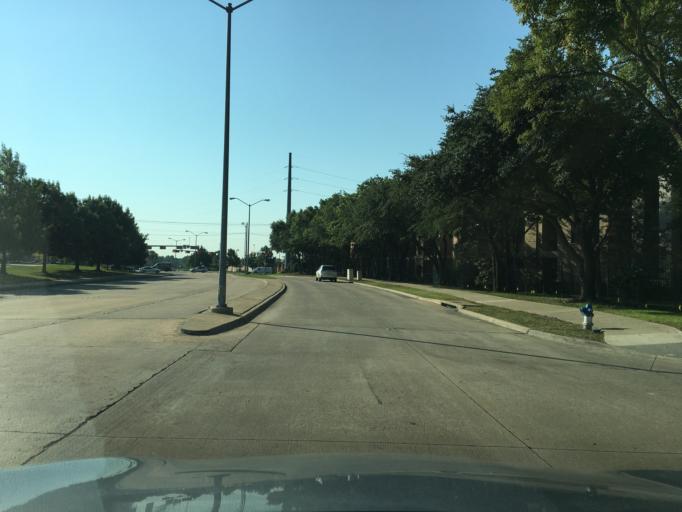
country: US
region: Texas
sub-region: Dallas County
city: Garland
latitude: 32.9625
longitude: -96.6485
